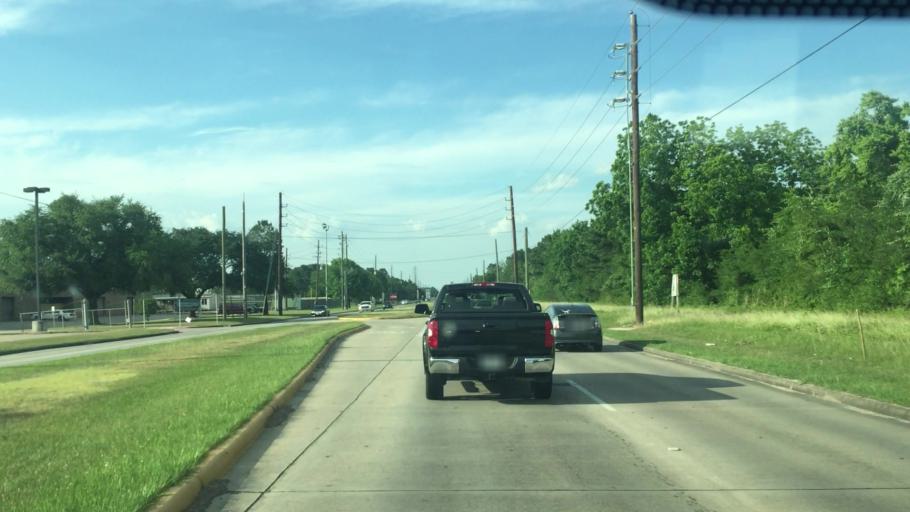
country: US
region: Texas
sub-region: Harris County
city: Hudson
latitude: 29.9645
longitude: -95.4975
